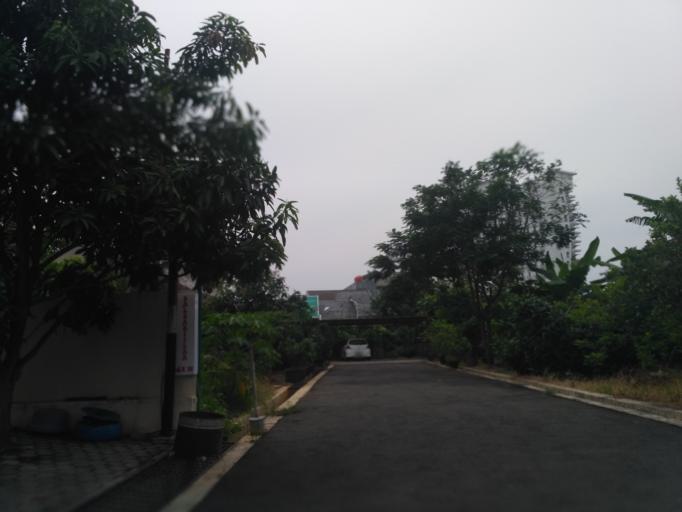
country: ID
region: Central Java
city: Semarang
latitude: -7.0577
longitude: 110.4306
